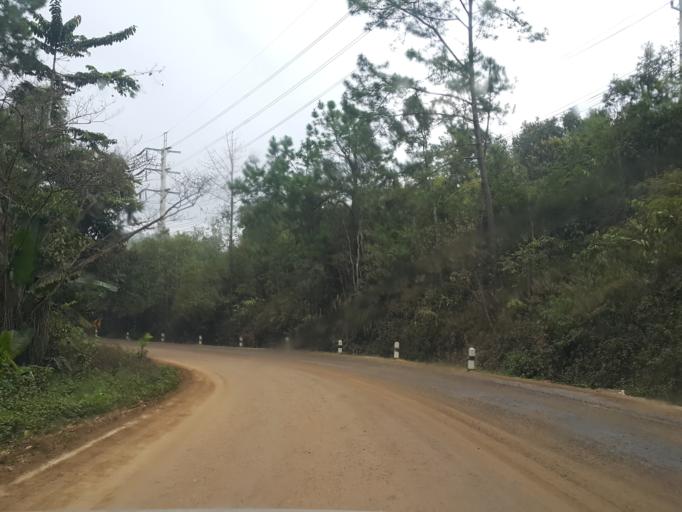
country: TH
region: Mae Hong Son
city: Mae Hi
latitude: 19.2705
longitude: 98.5781
